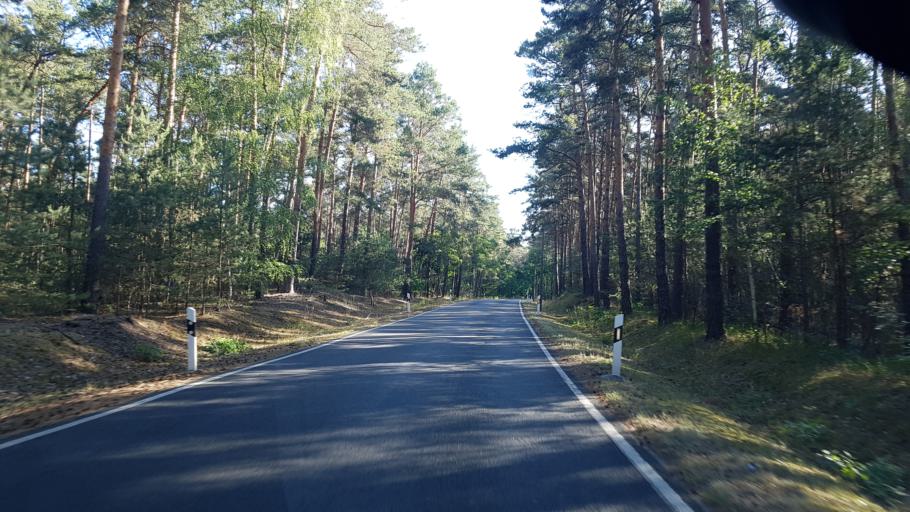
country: DE
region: Brandenburg
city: Kasel-Golzig
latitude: 51.9725
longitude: 13.6863
